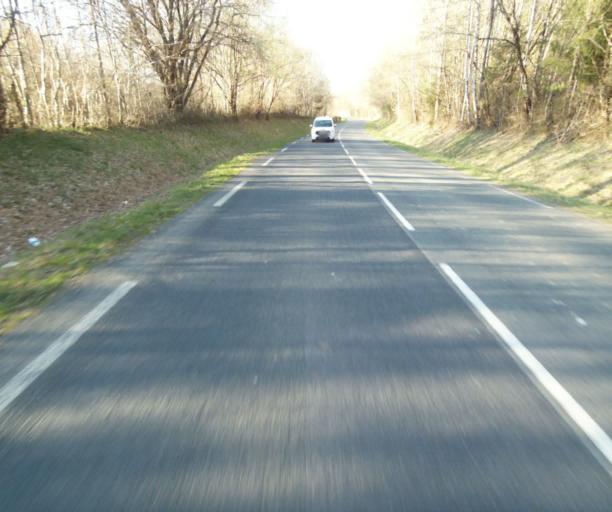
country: FR
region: Limousin
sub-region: Departement de la Correze
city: Seilhac
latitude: 45.3942
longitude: 1.7176
